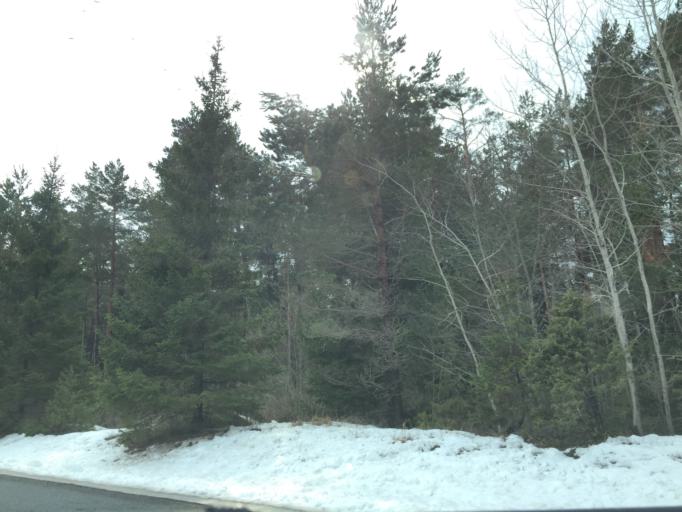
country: EE
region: Saare
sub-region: Kuressaare linn
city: Kuressaare
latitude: 58.4638
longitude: 22.0463
